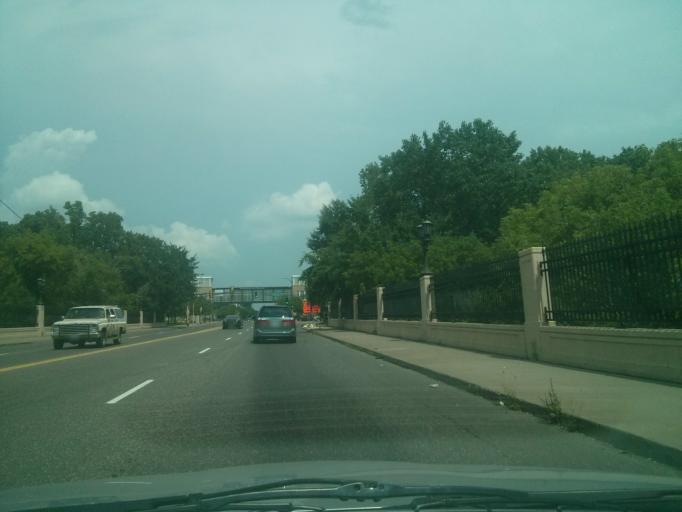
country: US
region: Minnesota
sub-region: Ramsey County
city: Saint Paul
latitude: 44.9564
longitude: -93.0771
